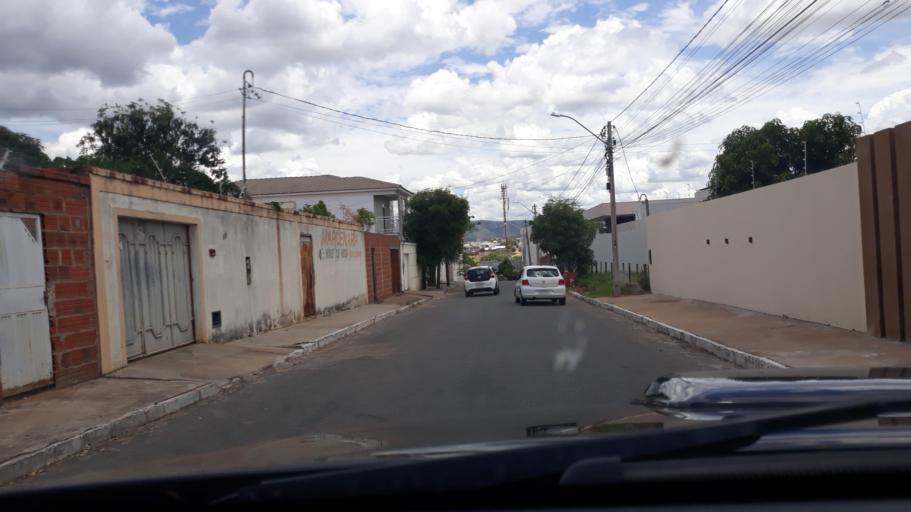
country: BR
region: Bahia
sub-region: Guanambi
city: Guanambi
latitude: -14.2261
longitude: -42.7705
